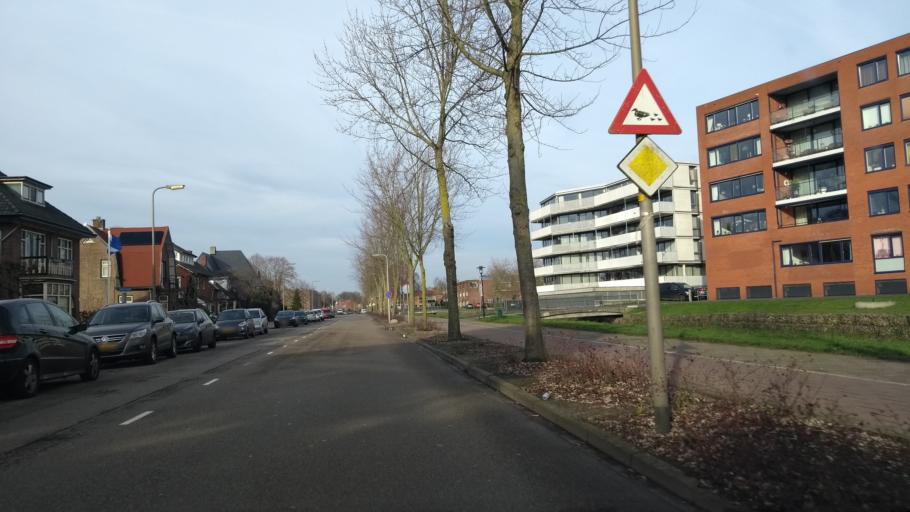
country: NL
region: Overijssel
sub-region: Gemeente Hengelo
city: Hengelo
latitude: 52.2678
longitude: 6.7860
